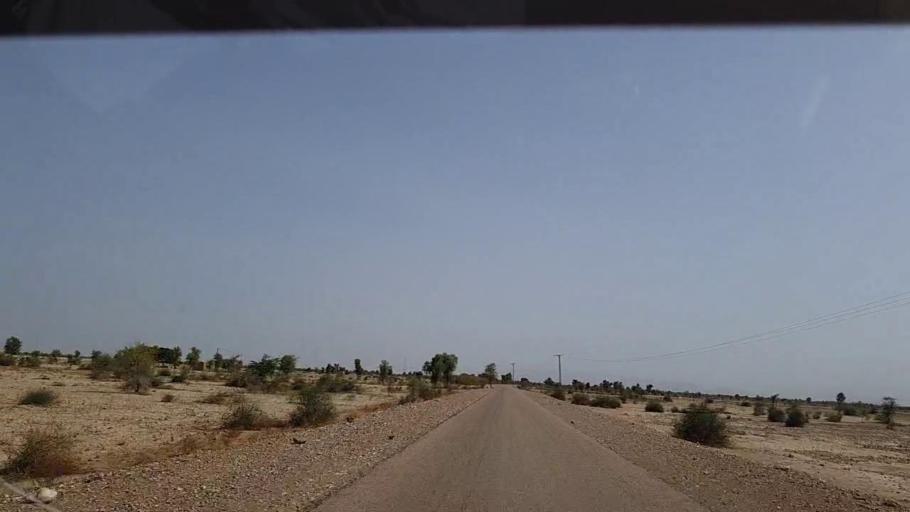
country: PK
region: Sindh
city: Johi
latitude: 26.6603
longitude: 67.5061
